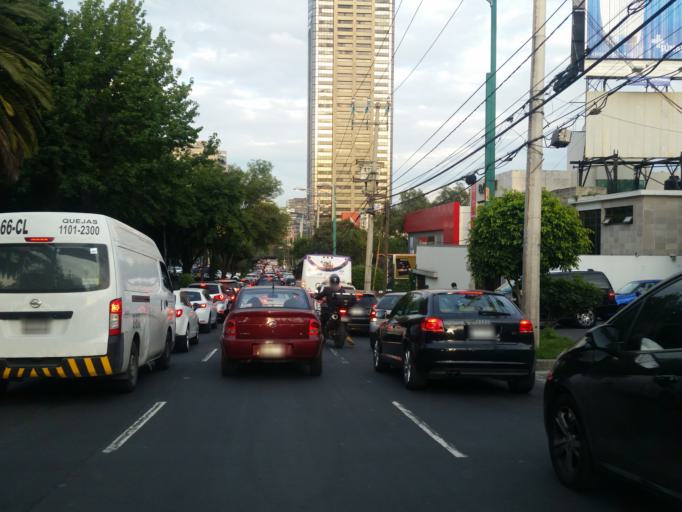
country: MX
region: Mexico City
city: Miguel Hidalgo
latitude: 19.4274
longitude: -99.2191
